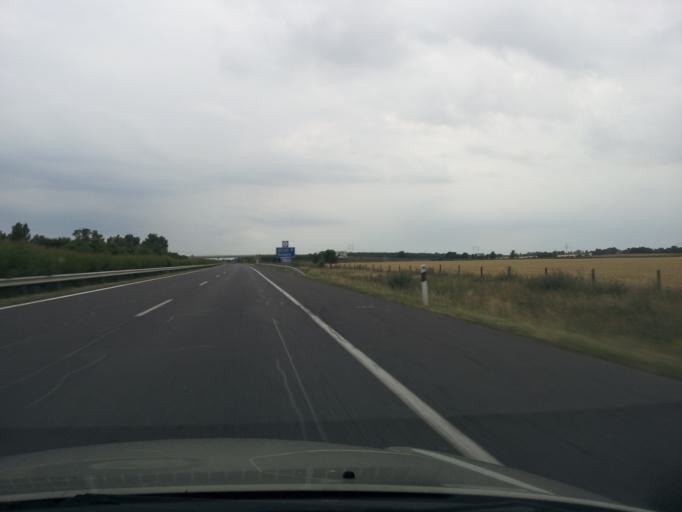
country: HU
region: Borsod-Abauj-Zemplen
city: Emod
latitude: 47.9029
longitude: 20.8370
